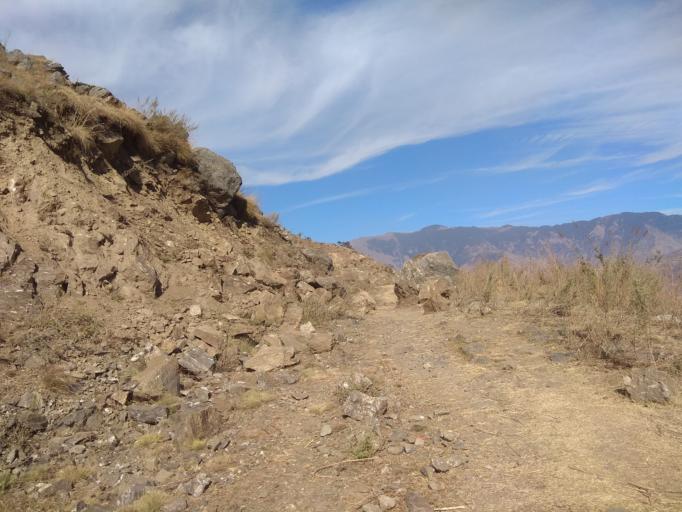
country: NP
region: Mid Western
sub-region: Bheri Zone
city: Dailekh
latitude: 29.3025
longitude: 81.7261
